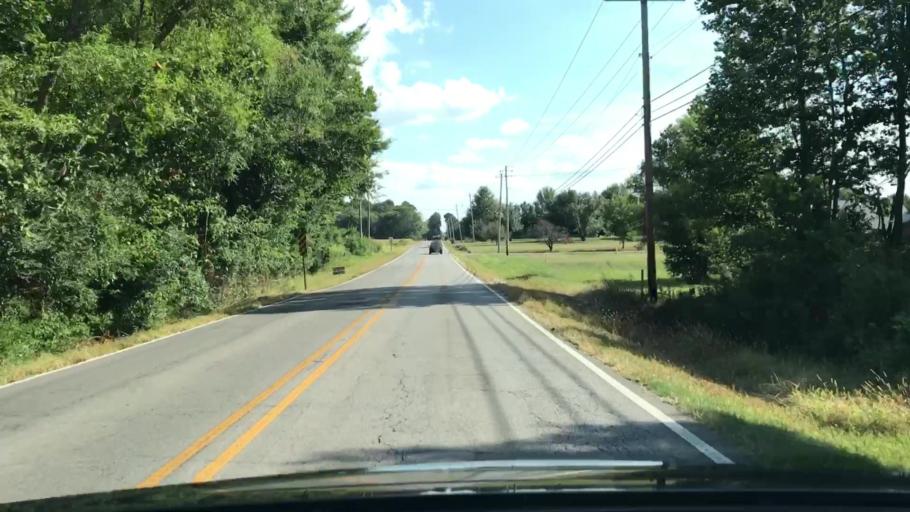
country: US
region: Alabama
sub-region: Madison County
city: Harvest
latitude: 34.8463
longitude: -86.7492
